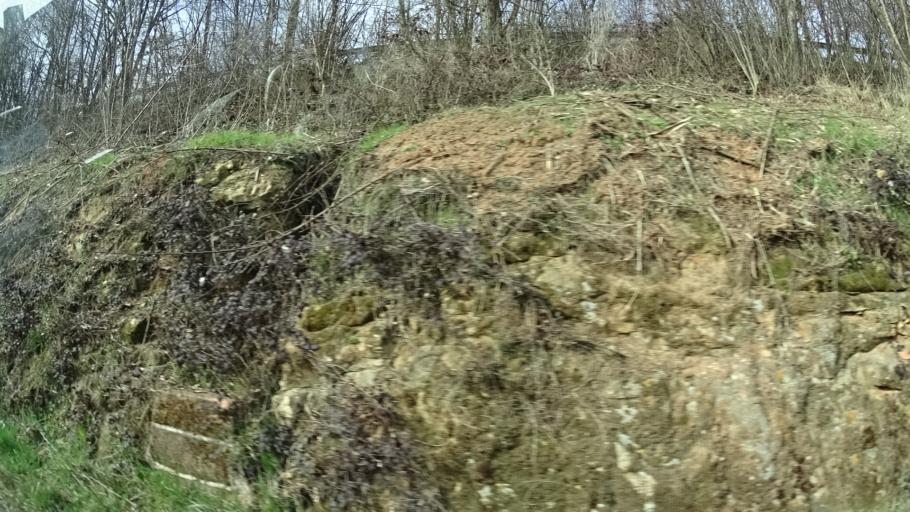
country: DE
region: Rheinland-Pfalz
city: Sankt Martin
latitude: 49.3009
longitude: 8.1002
